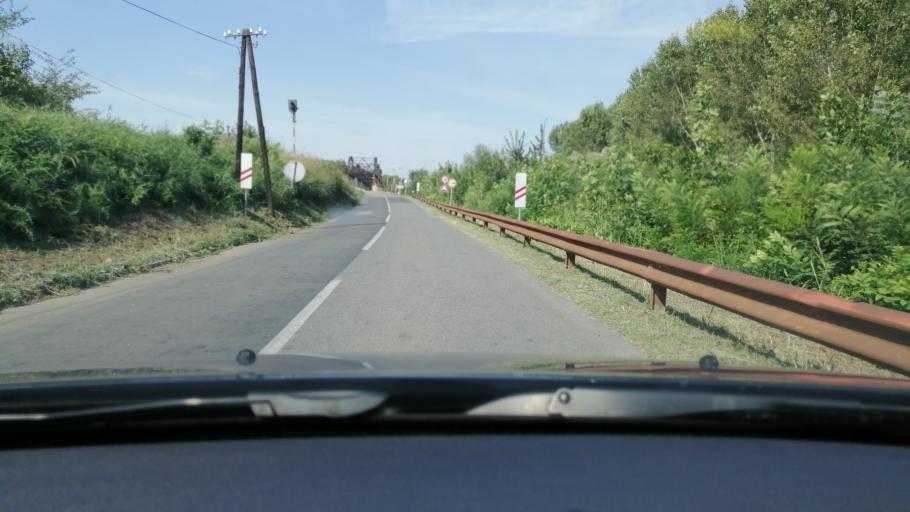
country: RS
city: Orlovat
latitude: 45.2492
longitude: 20.5976
